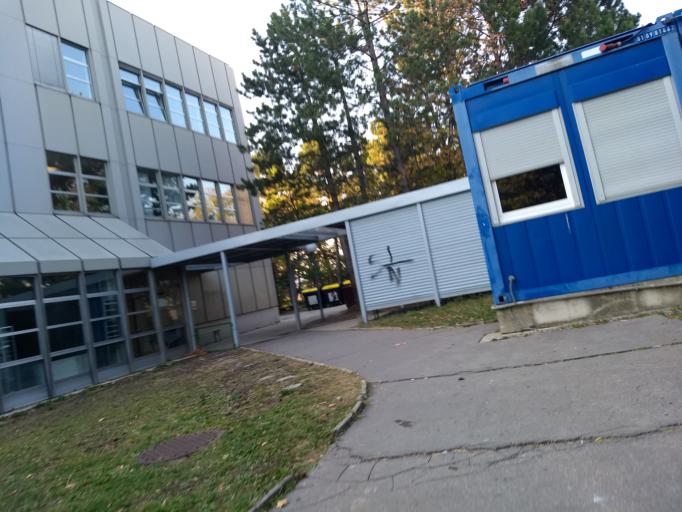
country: AT
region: Lower Austria
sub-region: Politischer Bezirk Modling
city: Perchtoldsdorf
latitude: 48.1210
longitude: 16.2611
